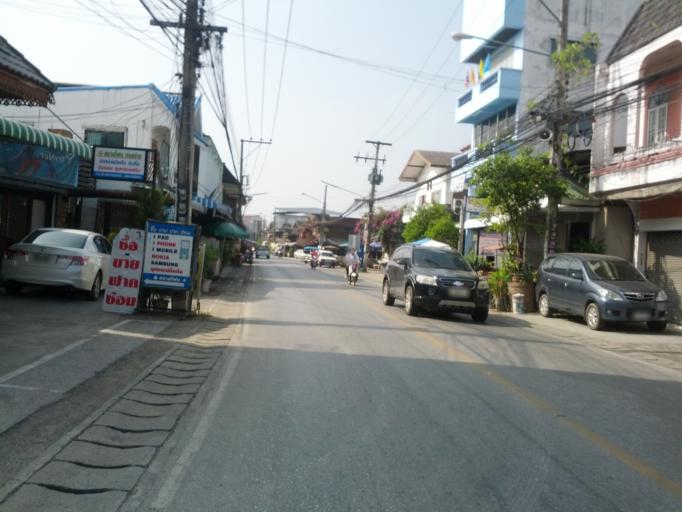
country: TH
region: Chiang Mai
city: San Kamphaeng
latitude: 18.7689
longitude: 99.0842
